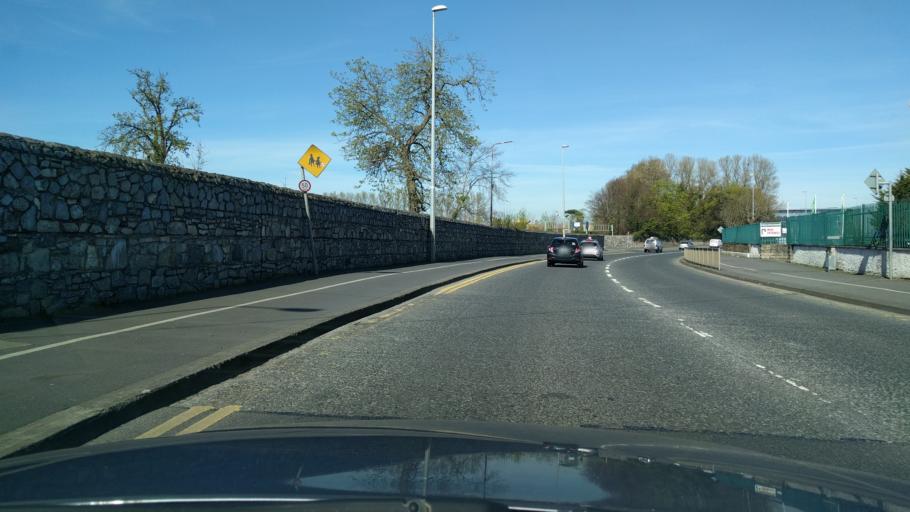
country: IE
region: Leinster
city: Tallaght
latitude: 53.2899
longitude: -6.3580
